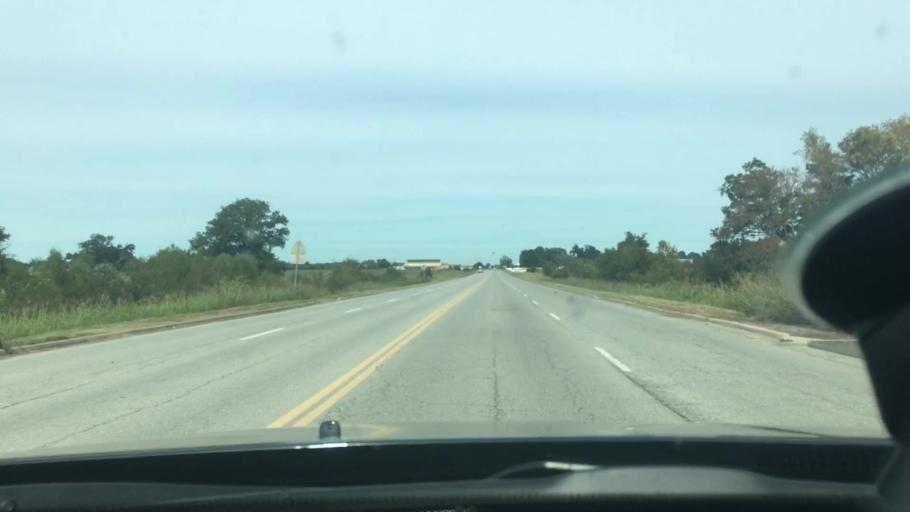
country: US
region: Oklahoma
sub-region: Atoka County
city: Atoka
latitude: 34.3851
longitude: -96.1455
